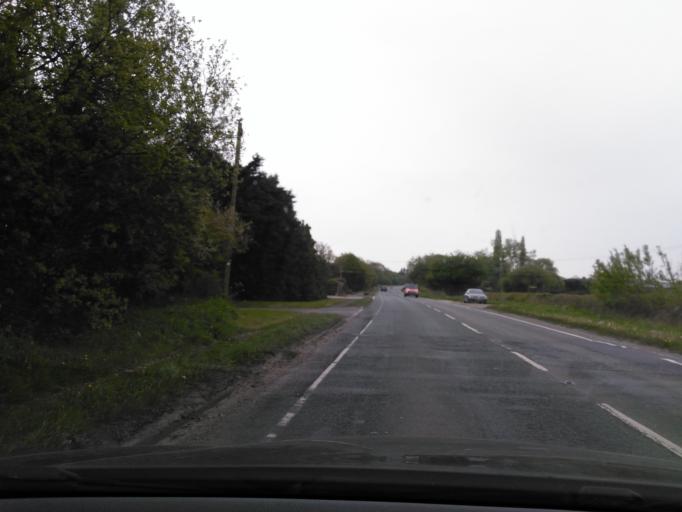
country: GB
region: England
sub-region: Hampshire
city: Tadley
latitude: 51.3368
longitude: -1.1279
